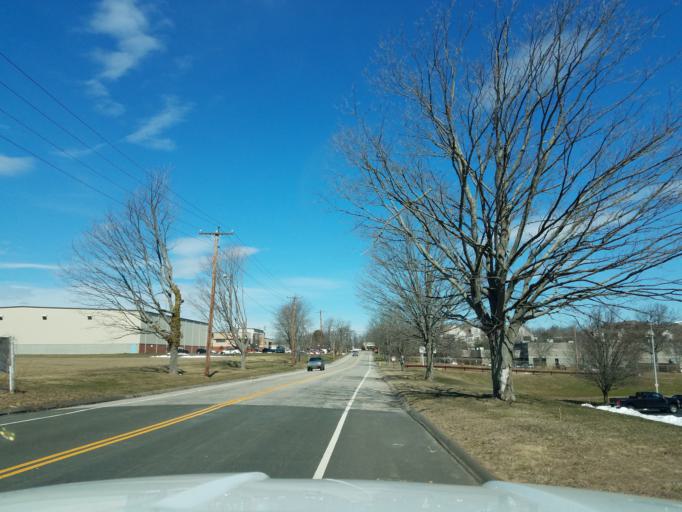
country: US
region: Connecticut
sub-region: New Haven County
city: Orange
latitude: 41.2617
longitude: -72.9965
